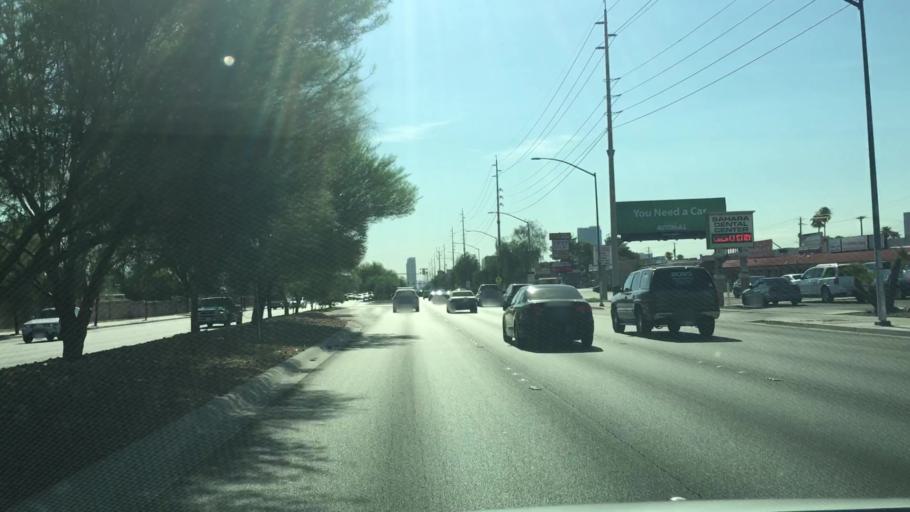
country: US
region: Nevada
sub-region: Clark County
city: Spring Valley
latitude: 36.1444
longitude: -115.1971
